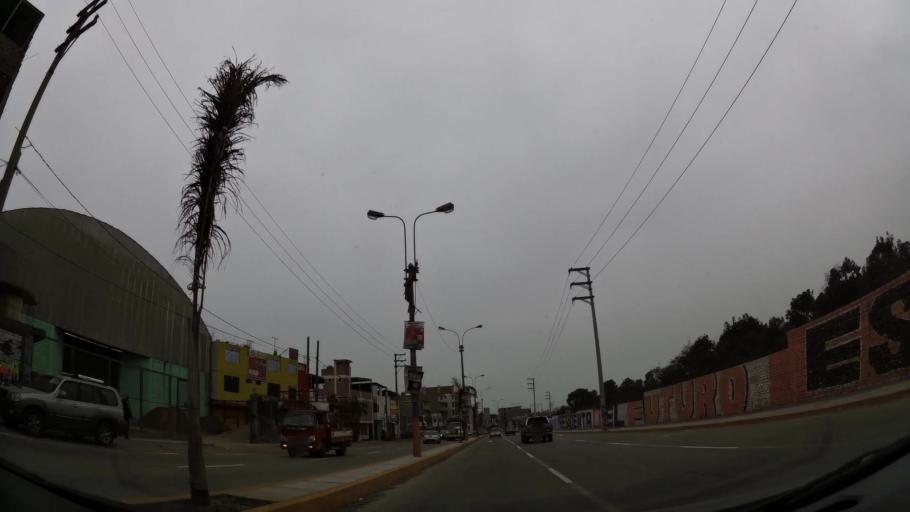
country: PE
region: Lima
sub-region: Lima
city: Surco
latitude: -12.1931
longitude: -76.9658
